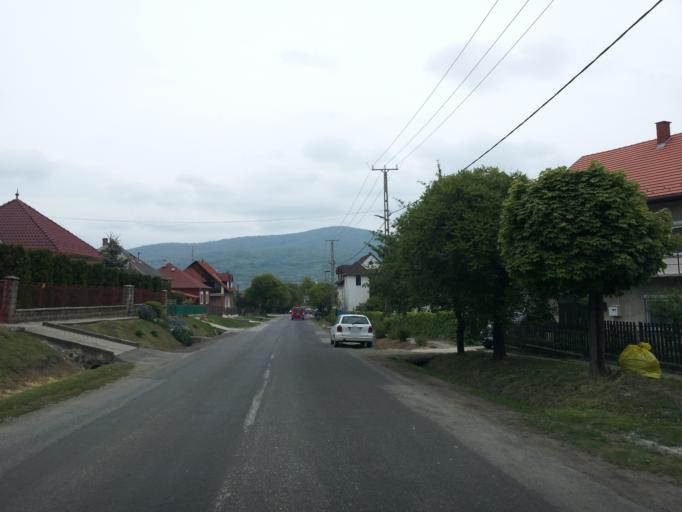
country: HU
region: Baranya
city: Hosszuheteny
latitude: 46.1495
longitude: 18.3542
